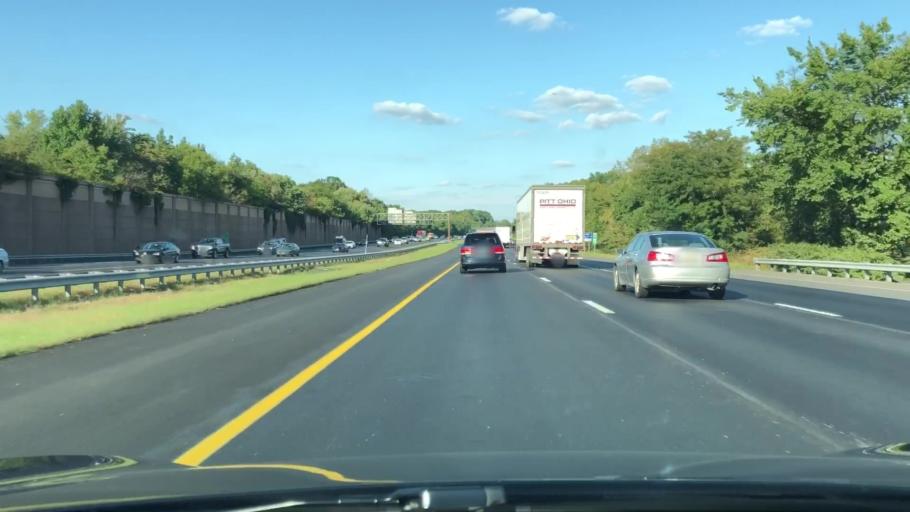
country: US
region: New Jersey
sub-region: Camden County
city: Ashland
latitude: 39.8848
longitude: -75.0060
